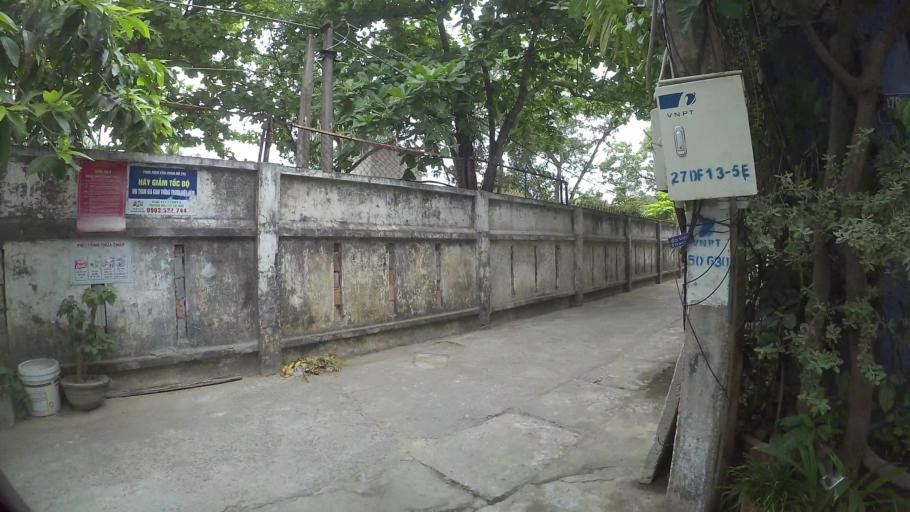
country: VN
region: Da Nang
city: Lien Chieu
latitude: 16.0760
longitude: 108.1714
